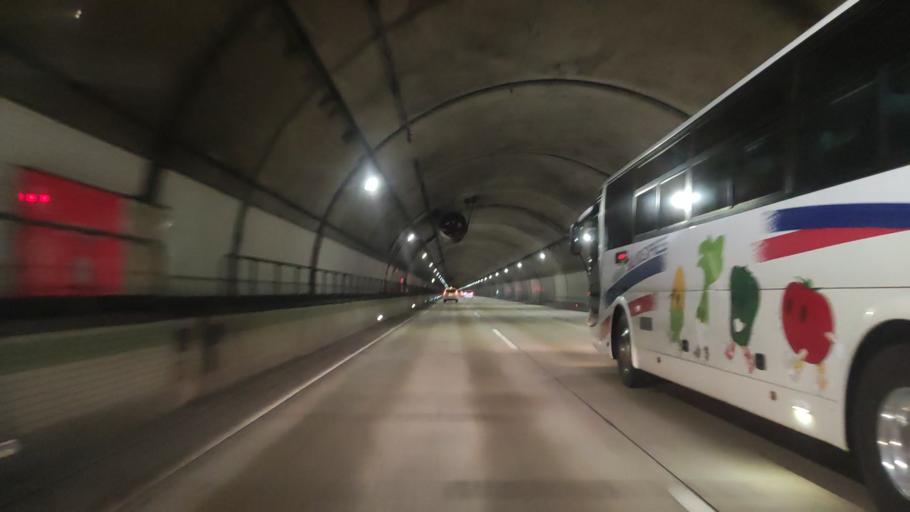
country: JP
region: Hyogo
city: Akashi
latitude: 34.6496
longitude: 135.0574
